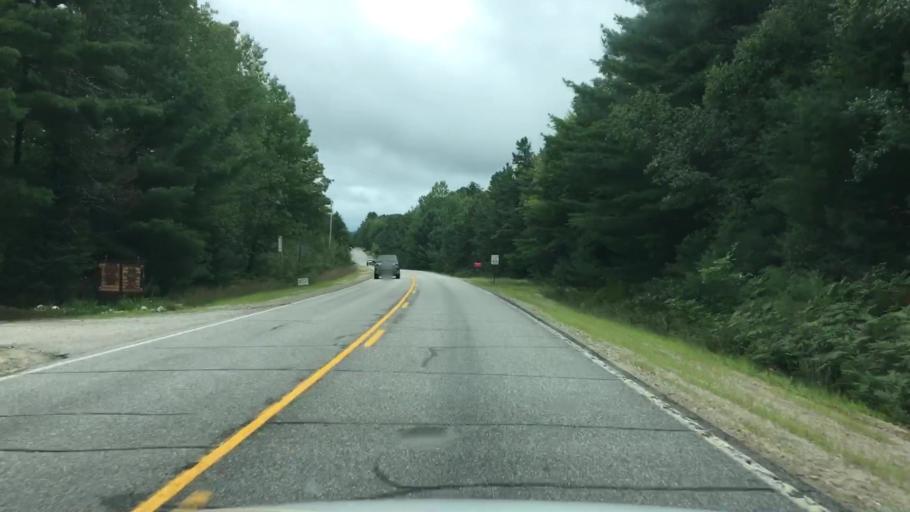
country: US
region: Maine
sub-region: Oxford County
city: Hiram
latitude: 43.9047
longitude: -70.8440
